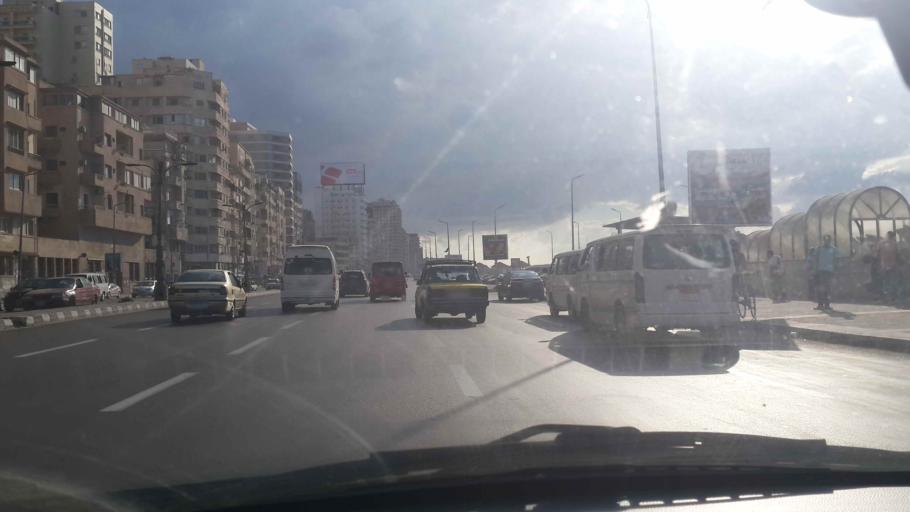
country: EG
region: Alexandria
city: Alexandria
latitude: 31.2187
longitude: 29.9269
